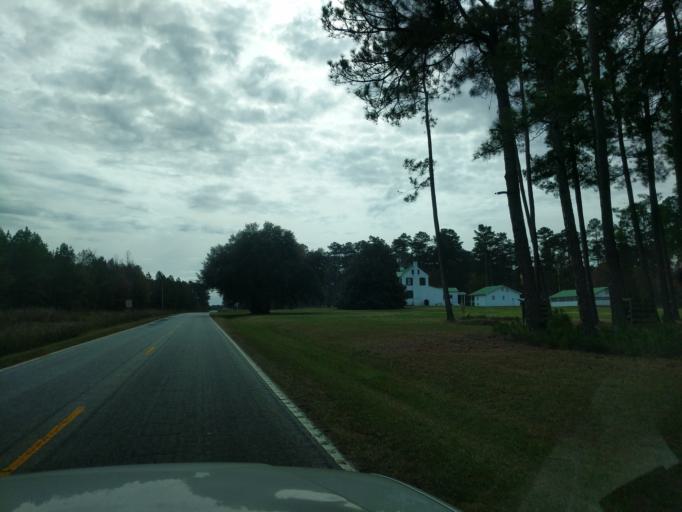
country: US
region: South Carolina
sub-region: Laurens County
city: Joanna
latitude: 34.3283
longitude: -81.8504
